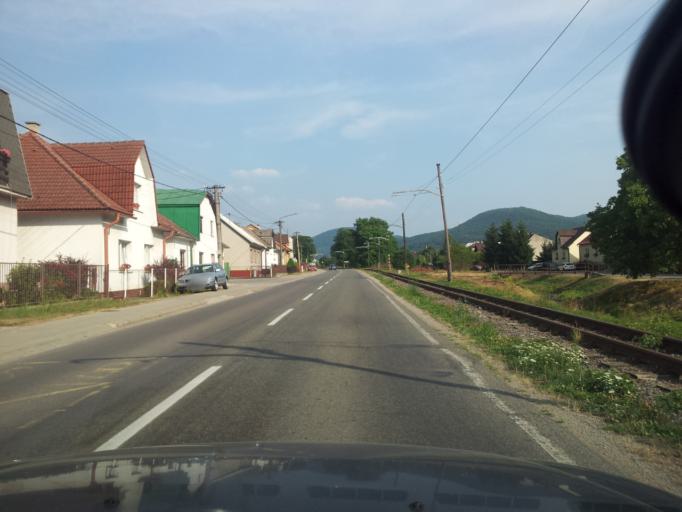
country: SK
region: Trenciansky
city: Nova Dubnica
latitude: 48.9291
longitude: 18.1304
